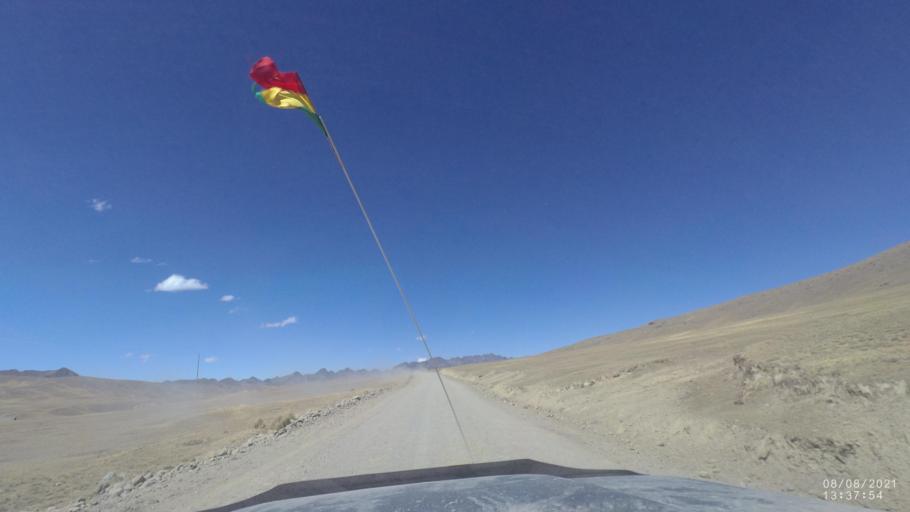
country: BO
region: Cochabamba
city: Colchani
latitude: -17.0832
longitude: -66.4926
